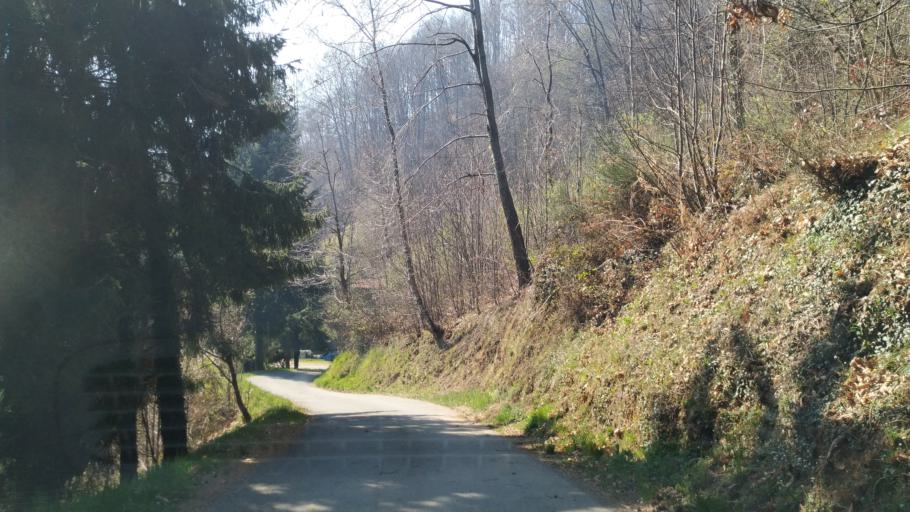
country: IT
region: Piedmont
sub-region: Provincia di Biella
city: Frazione Chiesa
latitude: 45.6888
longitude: 8.2008
